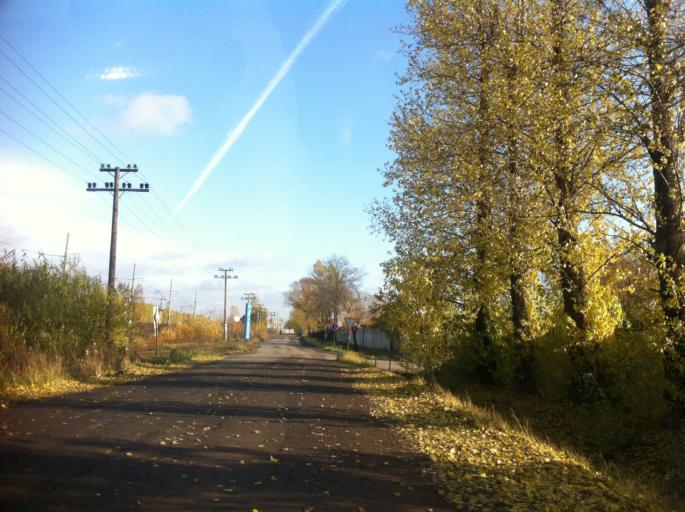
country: RU
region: St.-Petersburg
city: Sosnovaya Polyana
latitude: 59.8239
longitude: 30.1623
